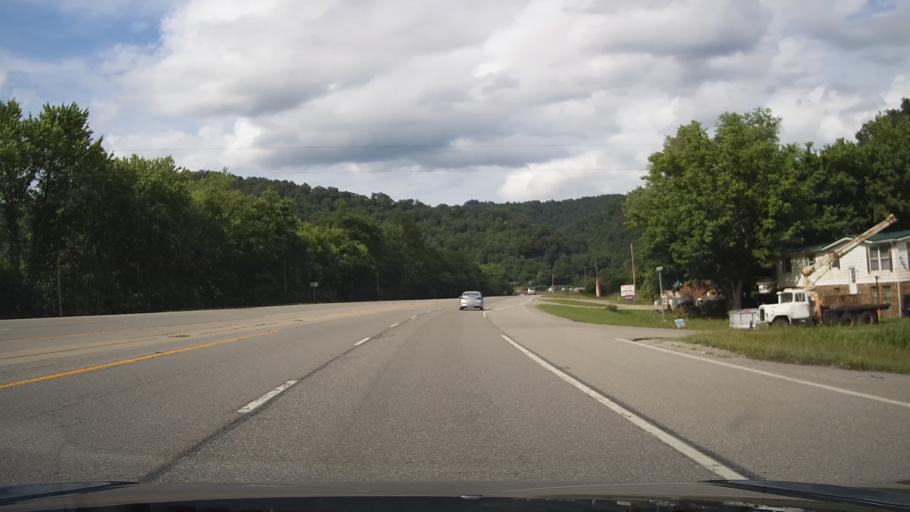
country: US
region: Kentucky
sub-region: Pike County
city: Coal Run Village
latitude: 37.5661
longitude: -82.6441
